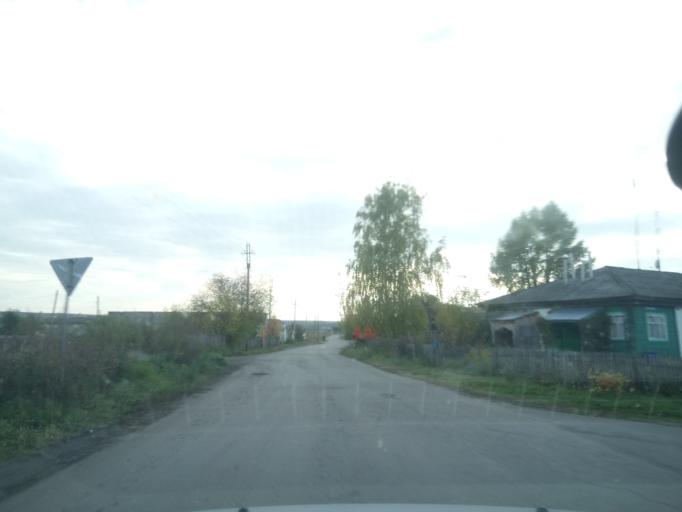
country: RU
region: Nizjnij Novgorod
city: Bol'shoye Boldino
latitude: 54.9940
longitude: 45.3109
